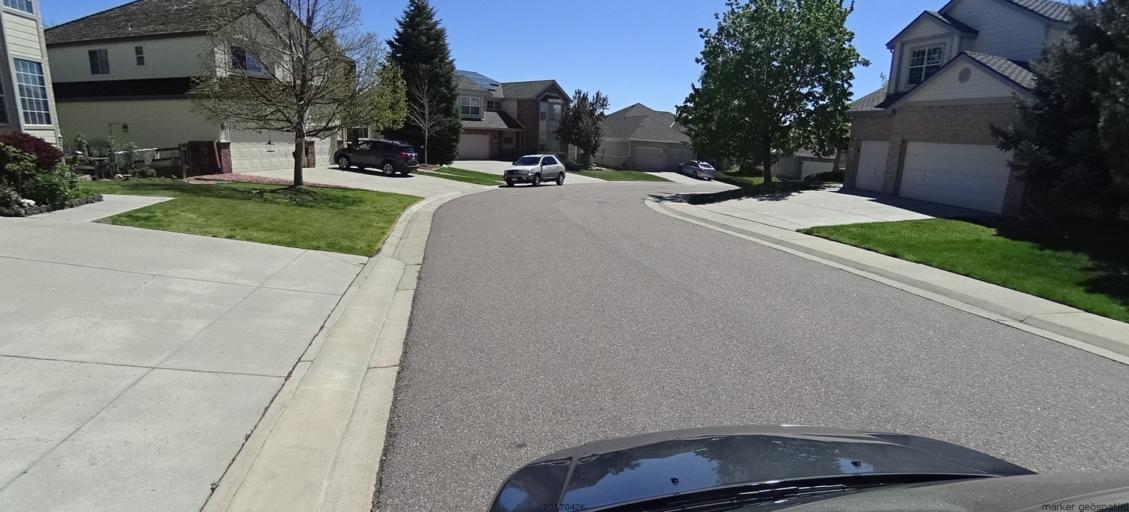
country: US
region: Colorado
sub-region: Adams County
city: Lone Tree
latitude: 39.5482
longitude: -104.8932
